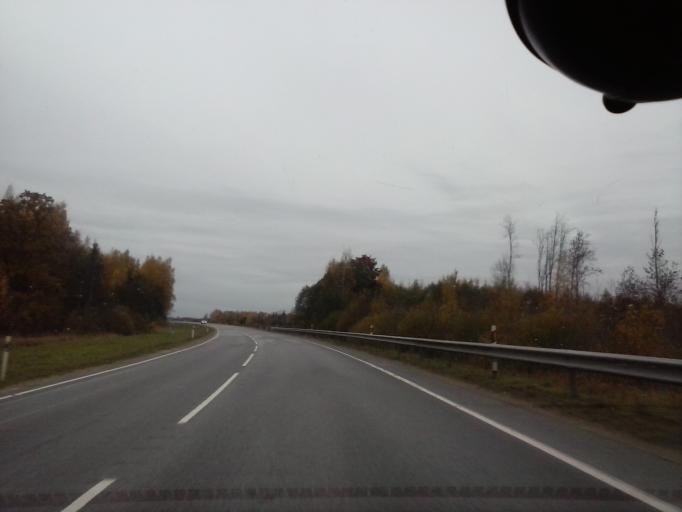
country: EE
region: Jogevamaa
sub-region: Jogeva linn
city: Jogeva
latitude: 58.5894
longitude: 26.2599
